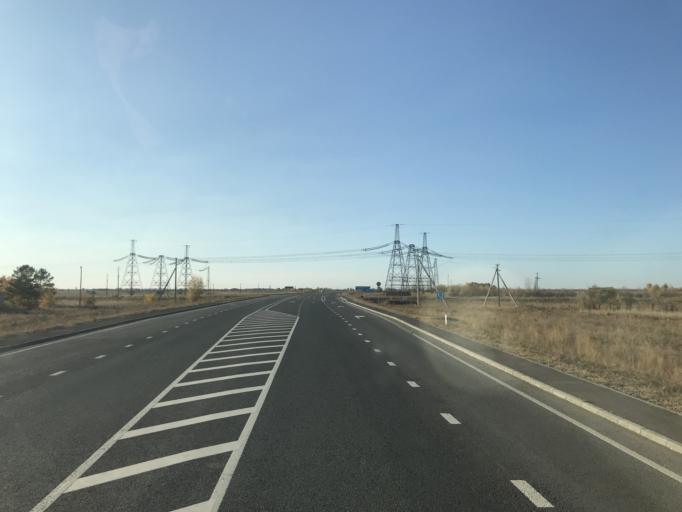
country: KZ
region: Pavlodar
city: Koktobe
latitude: 51.9082
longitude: 77.3615
